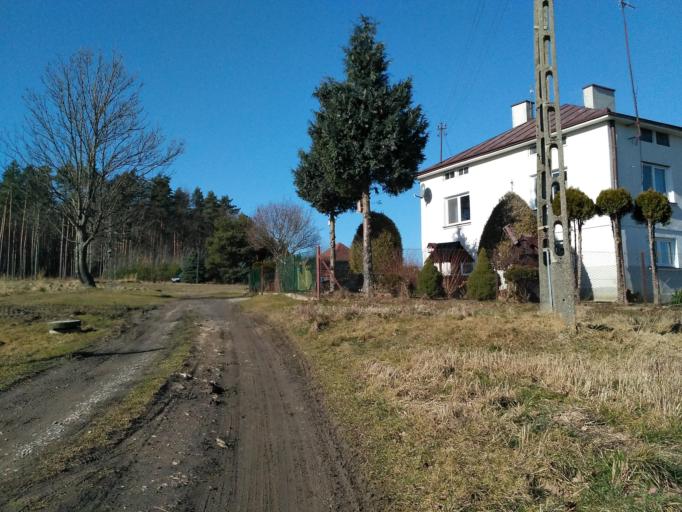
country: PL
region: Subcarpathian Voivodeship
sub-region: Powiat rzeszowski
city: Lutoryz
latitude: 49.9638
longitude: 21.8880
